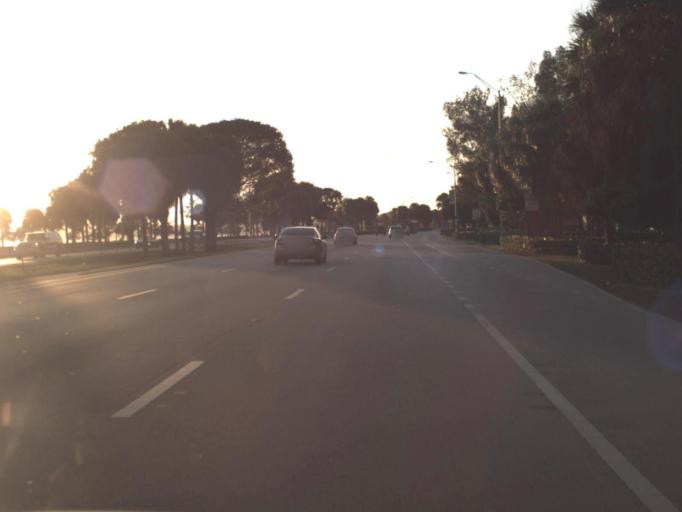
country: US
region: Florida
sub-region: Miami-Dade County
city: Miami
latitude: 25.7461
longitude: -80.1951
